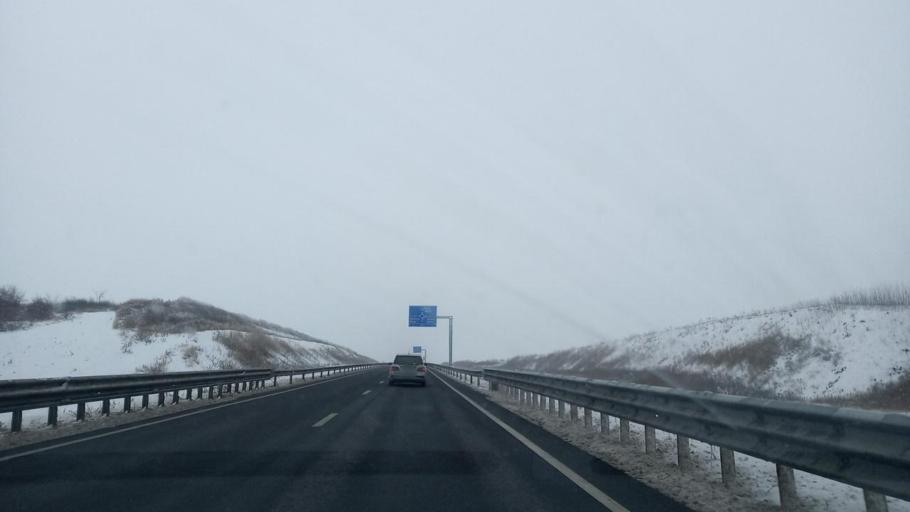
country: RO
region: Bacau
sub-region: Comuna Saucesti
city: Saucesti
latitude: 46.6372
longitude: 26.9214
